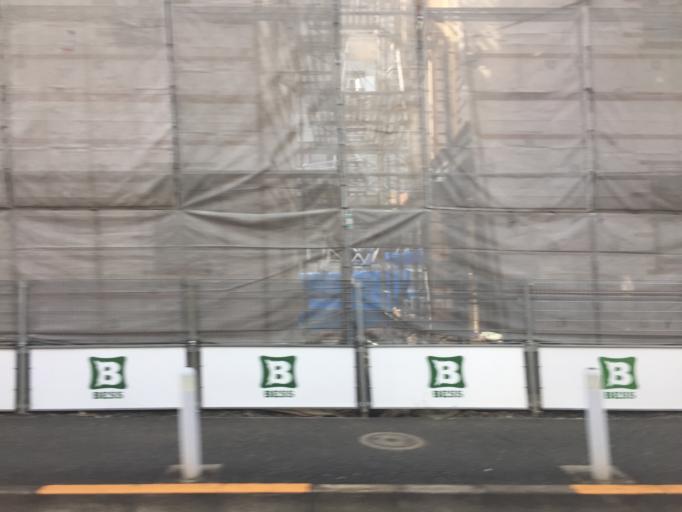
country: JP
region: Tokyo
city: Tokyo
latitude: 35.6133
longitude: 139.6480
